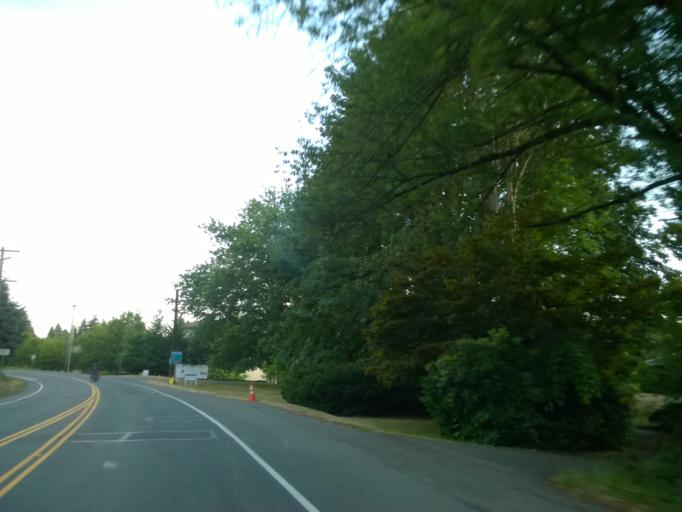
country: US
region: Washington
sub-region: King County
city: Woodinville
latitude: 47.7495
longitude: -122.1523
